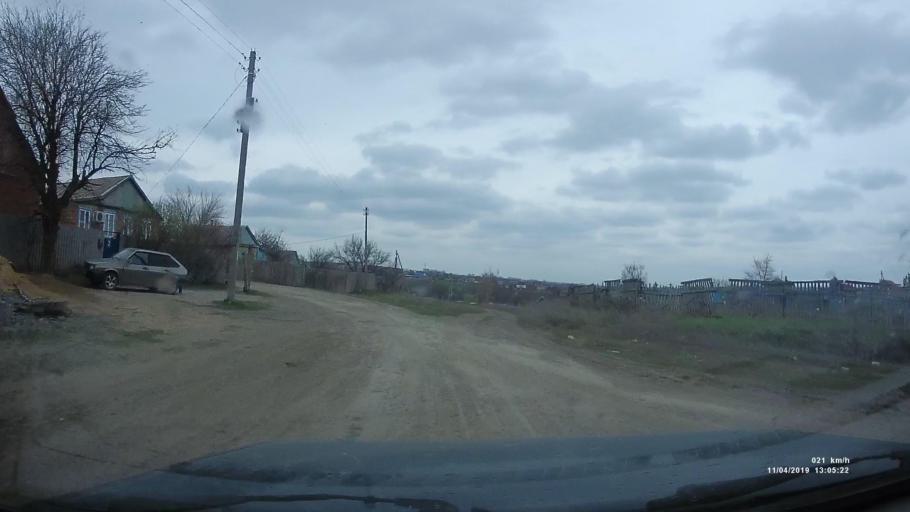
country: RU
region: Rostov
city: Staraya Stanitsa
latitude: 48.2866
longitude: 40.3429
